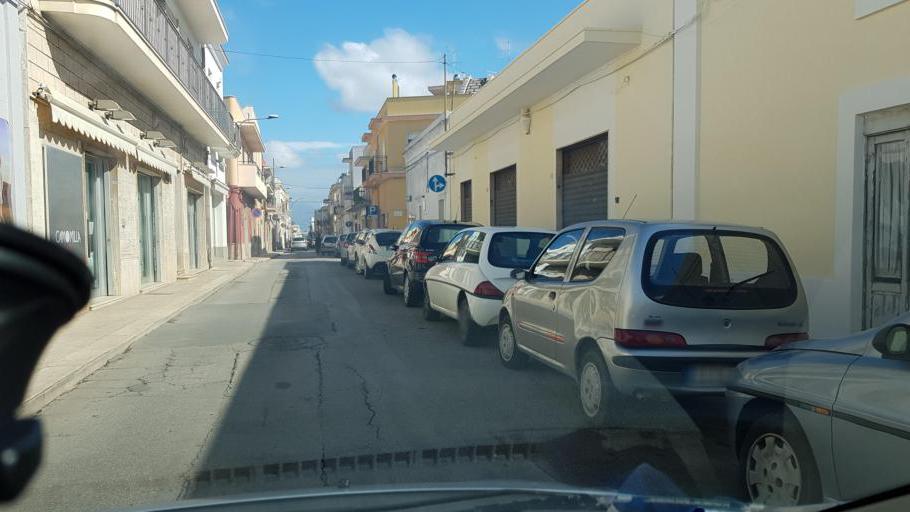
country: IT
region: Apulia
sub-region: Provincia di Brindisi
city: San Vito dei Normanni
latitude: 40.6573
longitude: 17.7087
